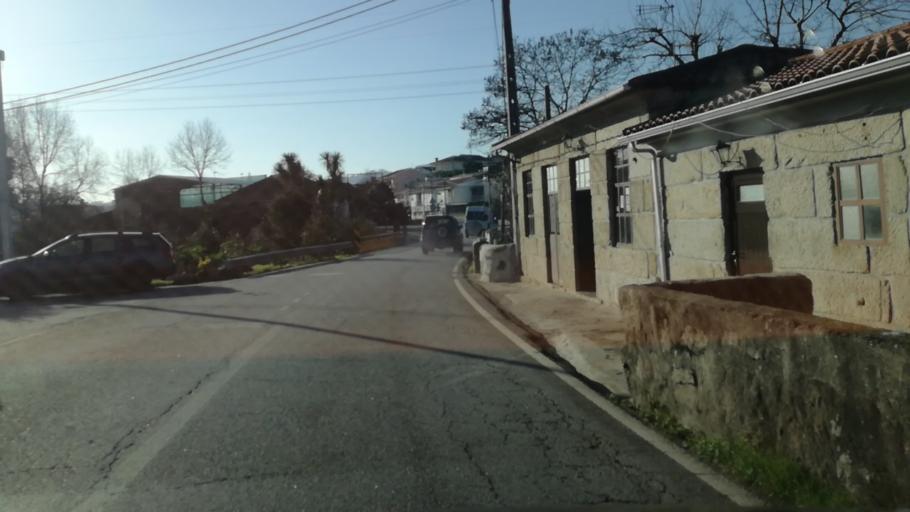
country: PT
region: Braga
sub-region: Guimaraes
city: Ponte
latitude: 41.4989
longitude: -8.3317
